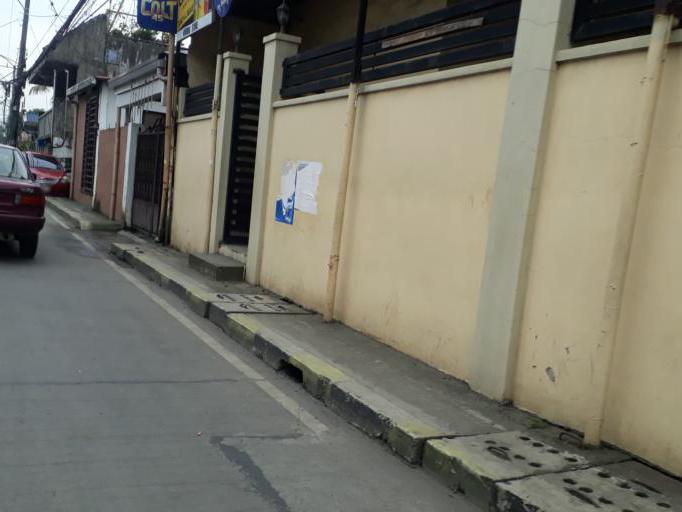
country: PH
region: Calabarzon
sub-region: Province of Rizal
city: Valenzuela
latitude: 14.7044
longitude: 120.9546
